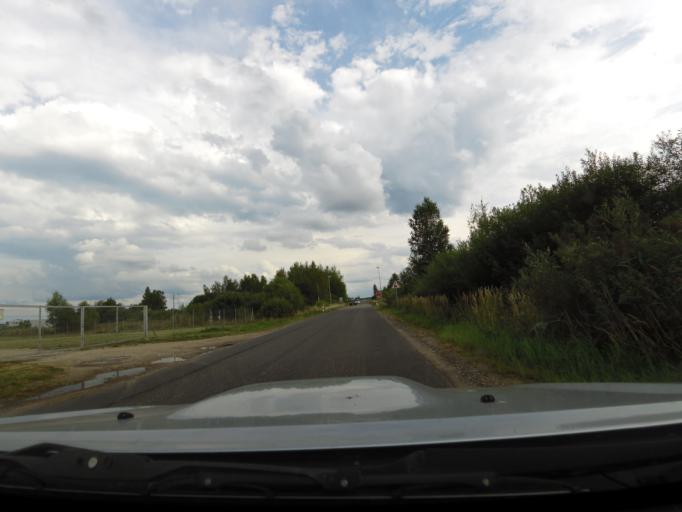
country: LT
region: Vilnius County
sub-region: Vilniaus Rajonas
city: Vievis
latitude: 54.7827
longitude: 24.8080
